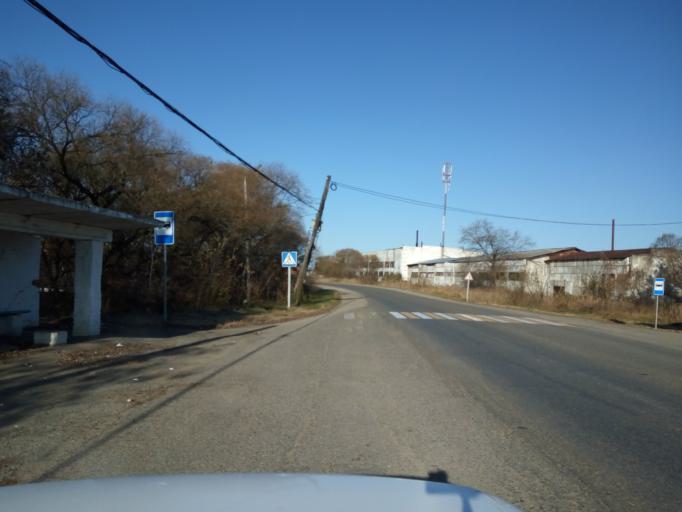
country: RU
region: Primorskiy
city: Dal'nerechensk
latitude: 45.9105
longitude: 133.8028
